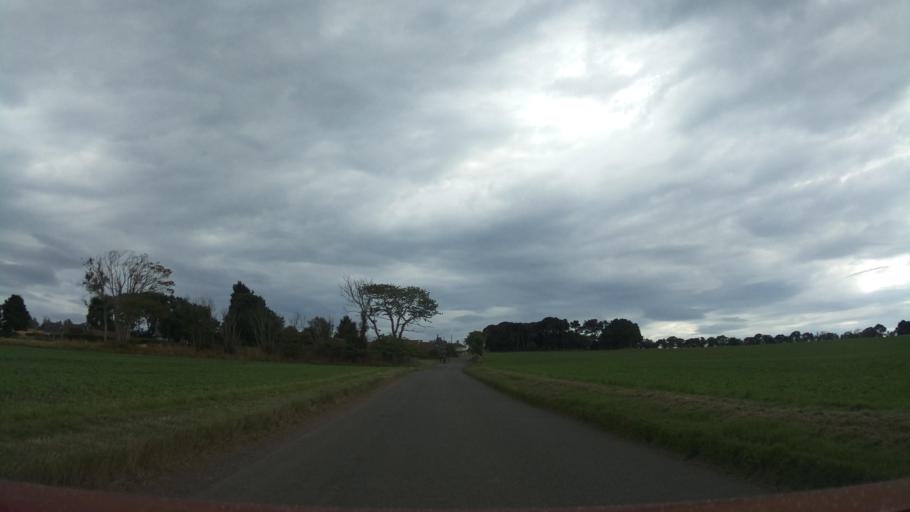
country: GB
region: Scotland
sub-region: Fife
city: Saint Andrews
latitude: 56.3227
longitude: -2.7805
